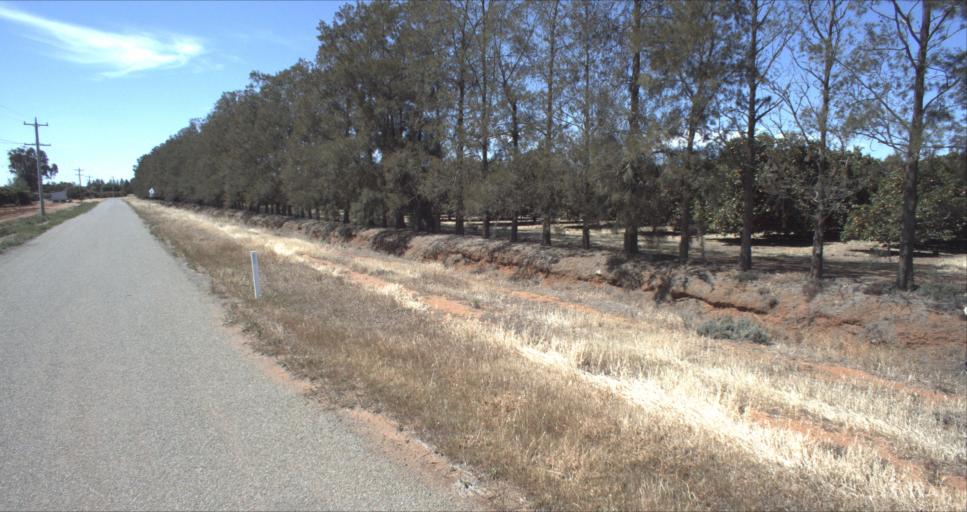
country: AU
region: New South Wales
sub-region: Leeton
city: Leeton
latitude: -34.6055
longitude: 146.4335
